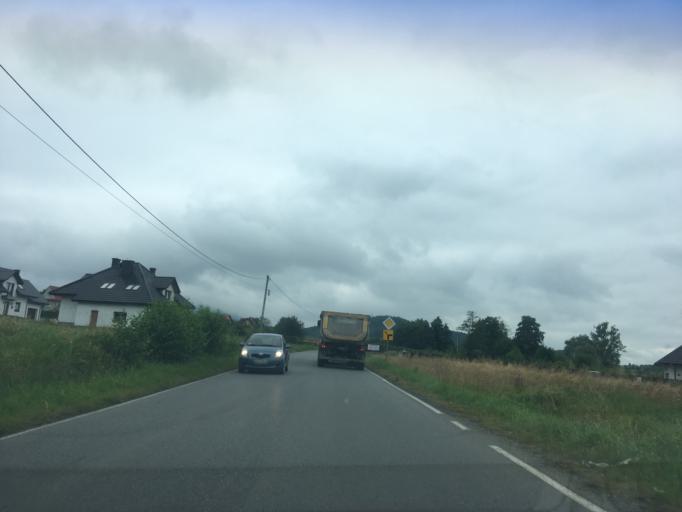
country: PL
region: Lesser Poland Voivodeship
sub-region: Powiat myslenicki
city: Trzemesnia
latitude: 49.8237
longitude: 20.0319
